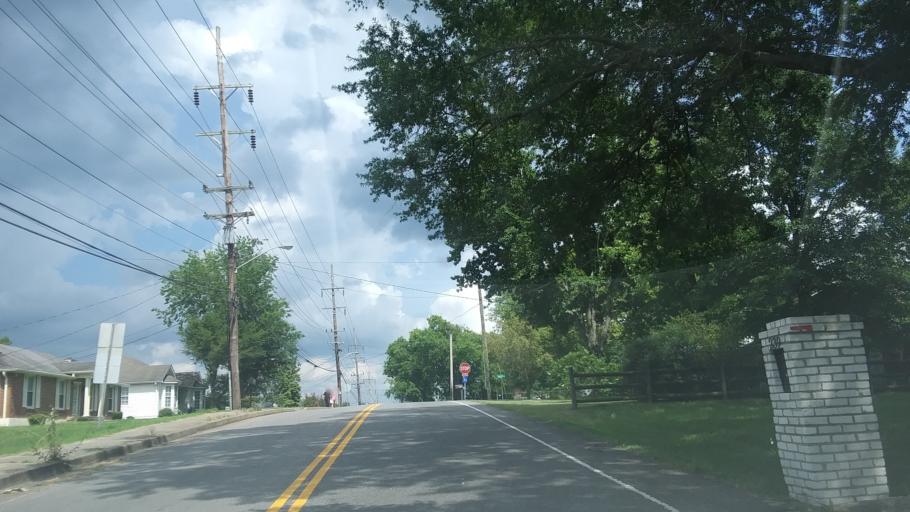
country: US
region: Tennessee
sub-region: Davidson County
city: Oak Hill
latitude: 36.0791
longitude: -86.7091
